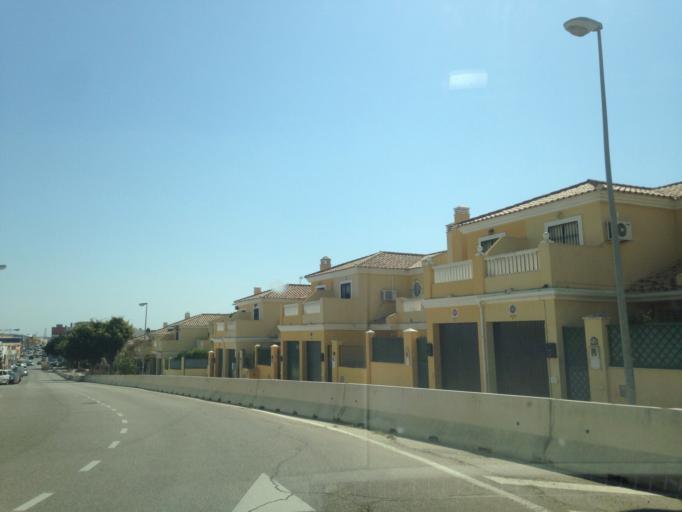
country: ES
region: Andalusia
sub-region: Provincia de Malaga
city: Malaga
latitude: 36.7013
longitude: -4.4762
